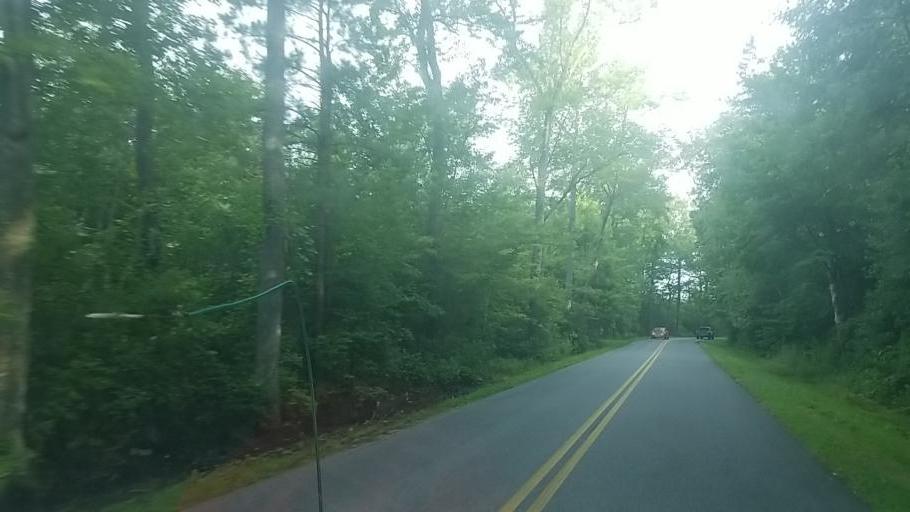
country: US
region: Maryland
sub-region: Worcester County
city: West Ocean City
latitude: 38.3292
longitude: -75.1554
